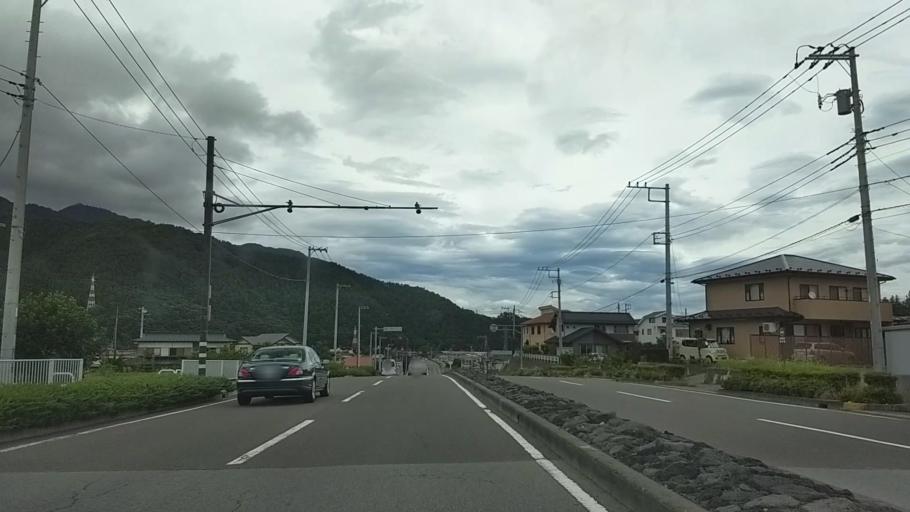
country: JP
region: Yamanashi
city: Fujikawaguchiko
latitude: 35.4969
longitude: 138.8164
